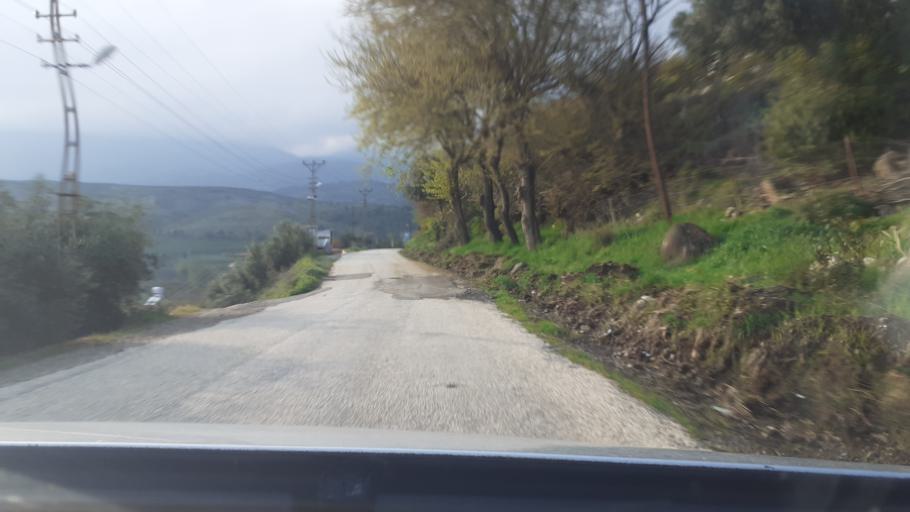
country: TR
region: Hatay
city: Kirikhan
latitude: 36.5019
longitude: 36.3263
